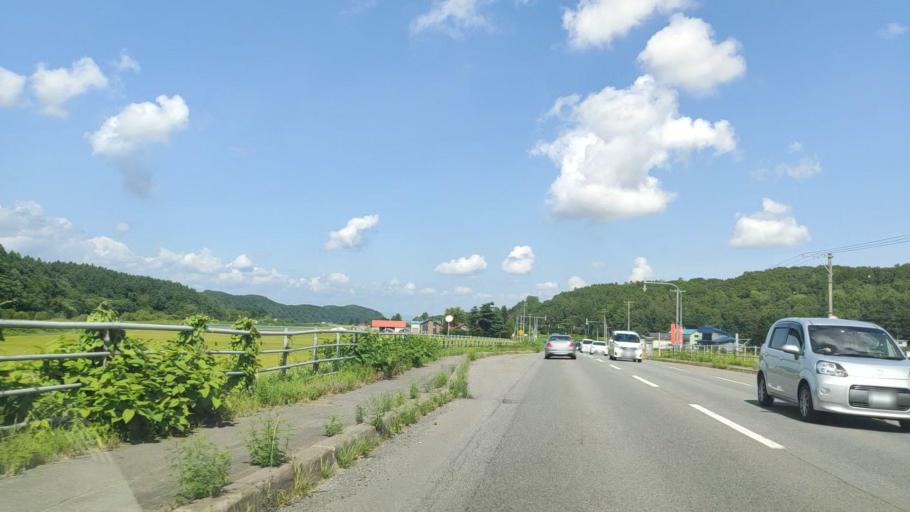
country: JP
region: Hokkaido
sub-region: Asahikawa-shi
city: Asahikawa
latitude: 43.6256
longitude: 142.4663
